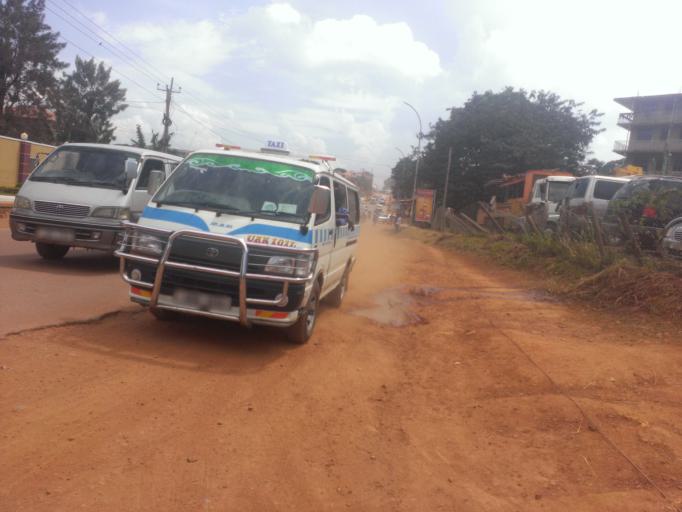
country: UG
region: Central Region
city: Kampala Central Division
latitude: 0.3246
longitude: 32.5658
